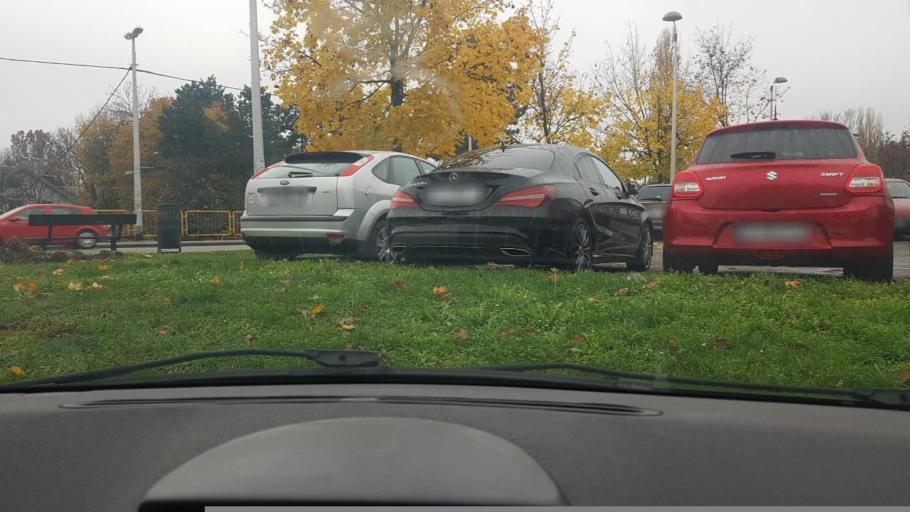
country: HR
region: Grad Zagreb
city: Zagreb
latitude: 45.8327
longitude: 15.9899
